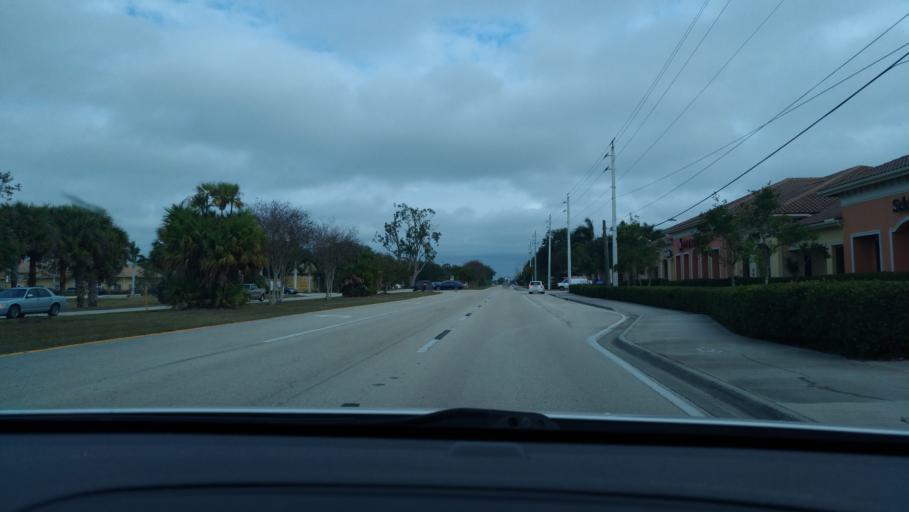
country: US
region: Florida
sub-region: Lee County
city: Estero
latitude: 26.4312
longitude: -81.8008
